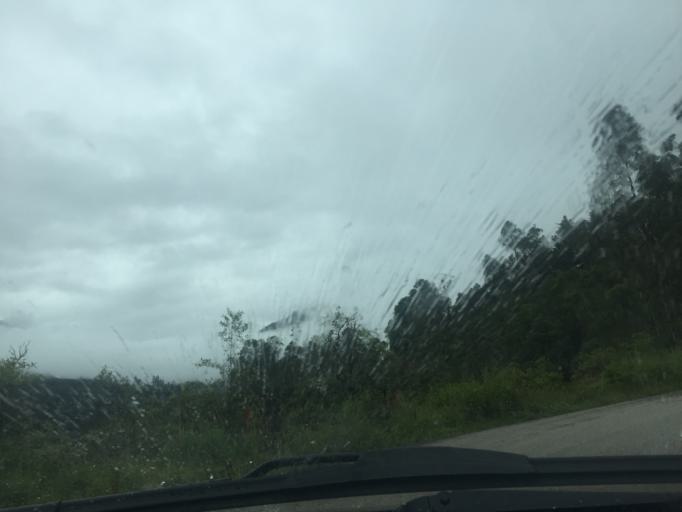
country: CO
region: Cundinamarca
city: Junin
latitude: 4.8096
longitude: -73.7186
